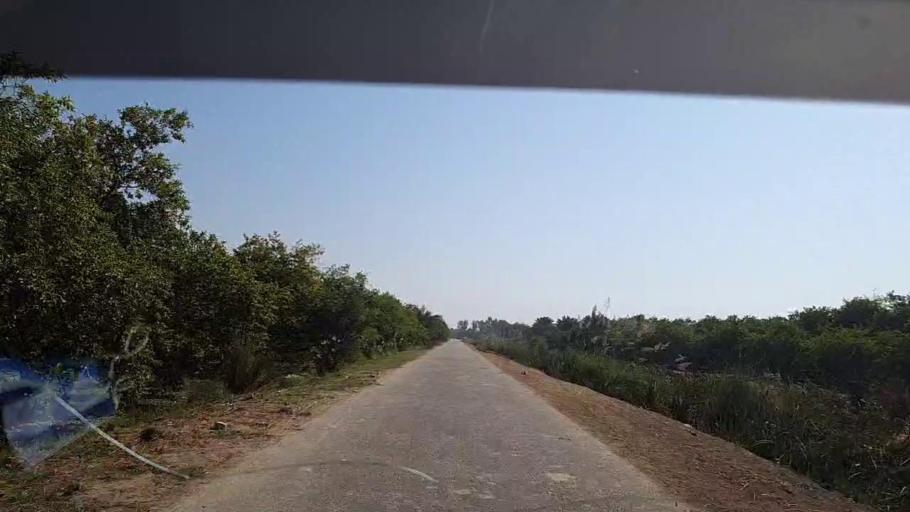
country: PK
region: Sindh
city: Larkana
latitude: 27.6034
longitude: 68.2634
